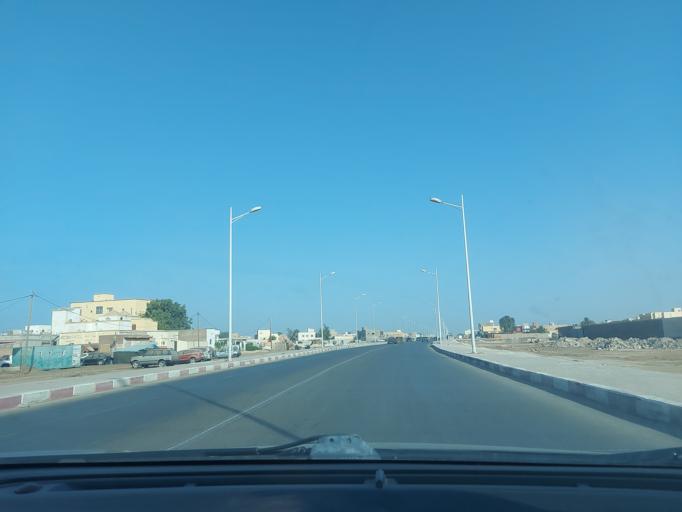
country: MR
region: Nouakchott
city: Nouakchott
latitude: 18.0851
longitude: -16.0007
